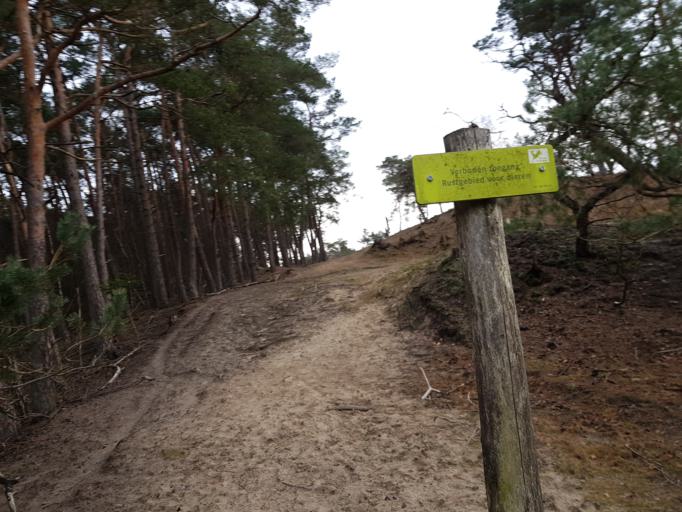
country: NL
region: Utrecht
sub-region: Gemeente Utrechtse Heuvelrug
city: Driebergen-Rijsenburg
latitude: 52.0774
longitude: 5.2986
